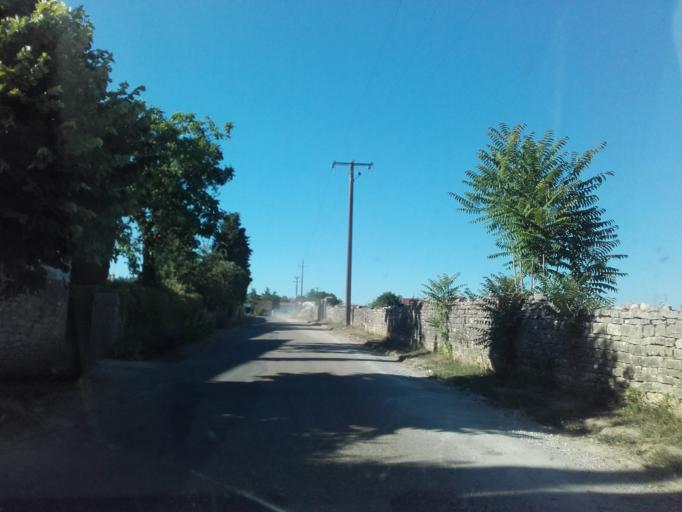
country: FR
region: Bourgogne
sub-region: Departement de Saone-et-Loire
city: Mellecey
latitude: 46.8327
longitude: 4.7345
